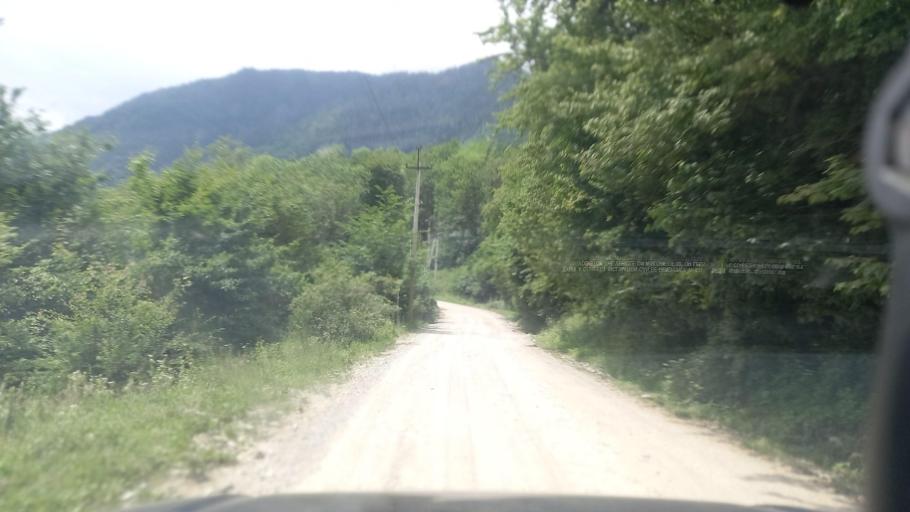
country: RU
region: Karachayevo-Cherkesiya
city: Kurdzhinovo
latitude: 43.9039
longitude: 40.9489
